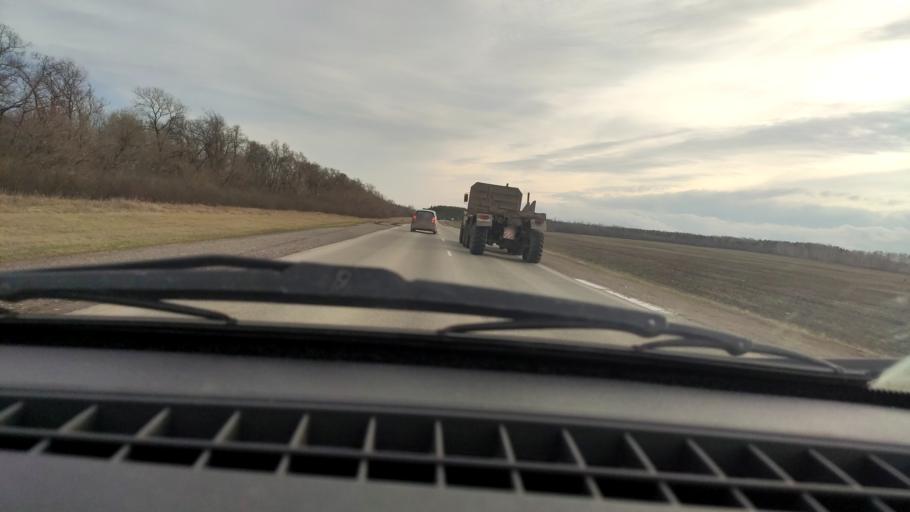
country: RU
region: Bashkortostan
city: Davlekanovo
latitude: 54.2531
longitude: 55.0829
